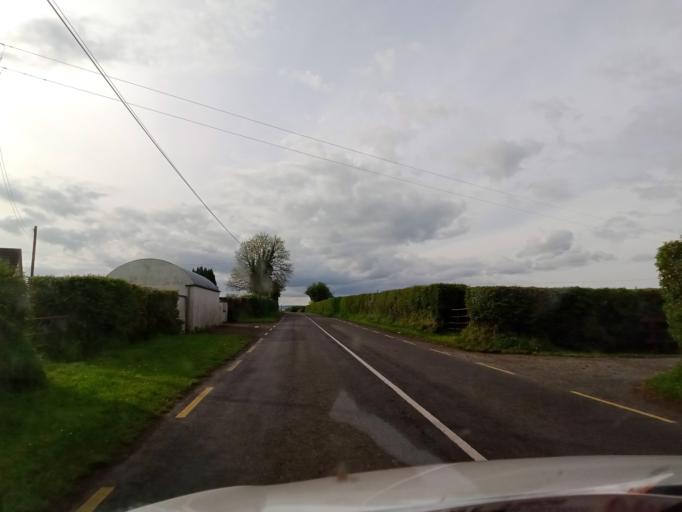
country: IE
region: Leinster
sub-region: Laois
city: Abbeyleix
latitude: 52.9581
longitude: -7.4038
